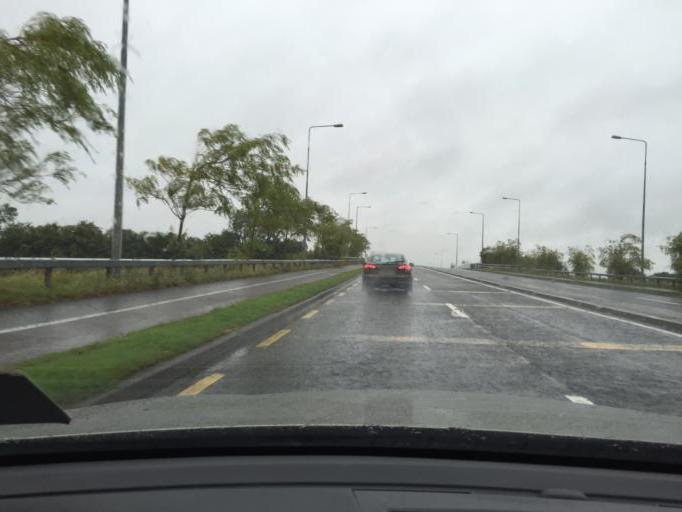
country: IE
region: Leinster
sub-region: Kildare
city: Leixlip
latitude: 53.3689
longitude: -6.5217
